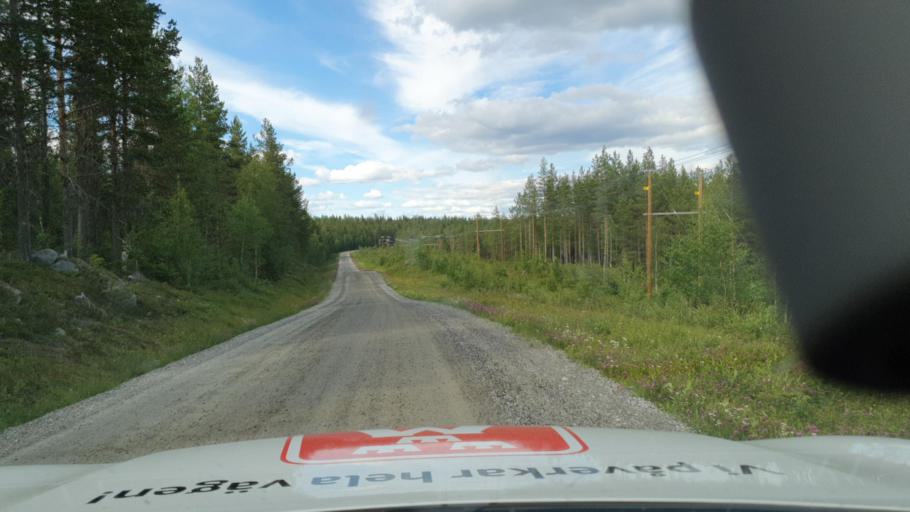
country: SE
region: Vaesterbotten
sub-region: Asele Kommun
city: Insjon
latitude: 64.2123
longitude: 17.8114
